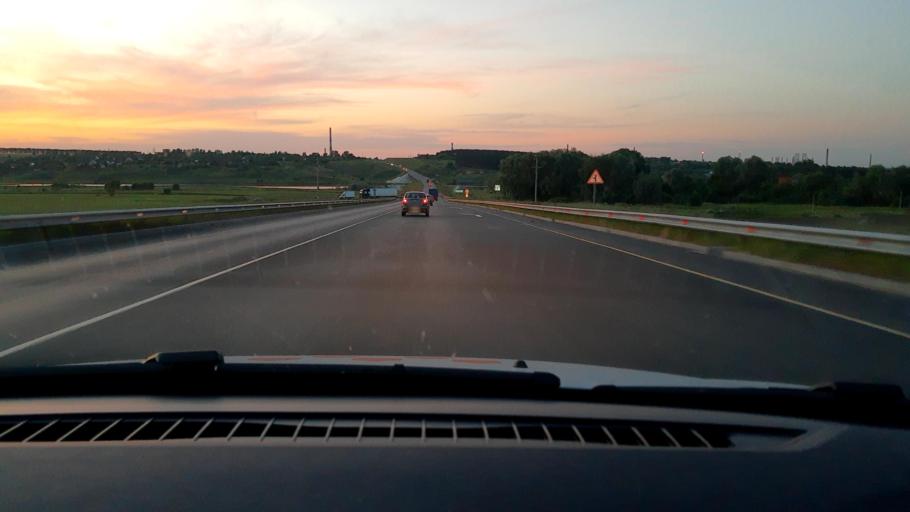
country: RU
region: Nizjnij Novgorod
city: Kstovo
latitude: 56.0696
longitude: 44.1302
